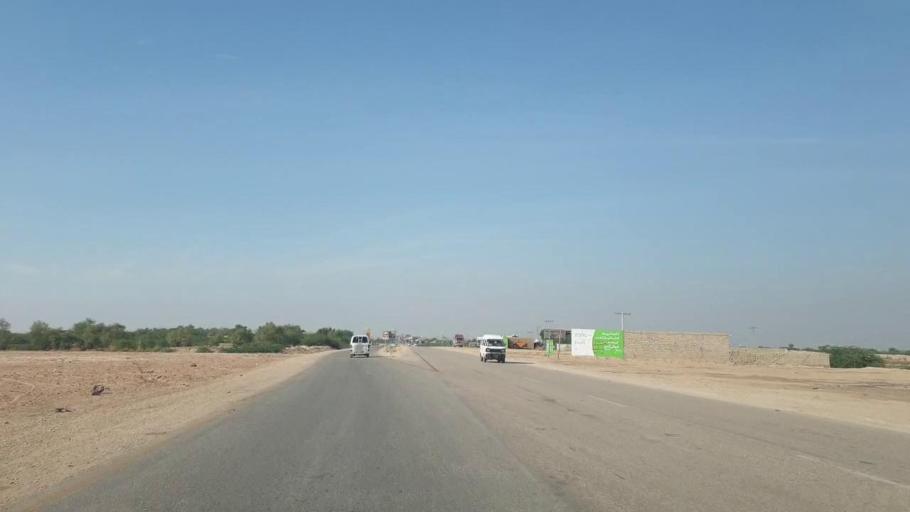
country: PK
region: Sindh
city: Sehwan
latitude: 26.3894
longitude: 67.8687
